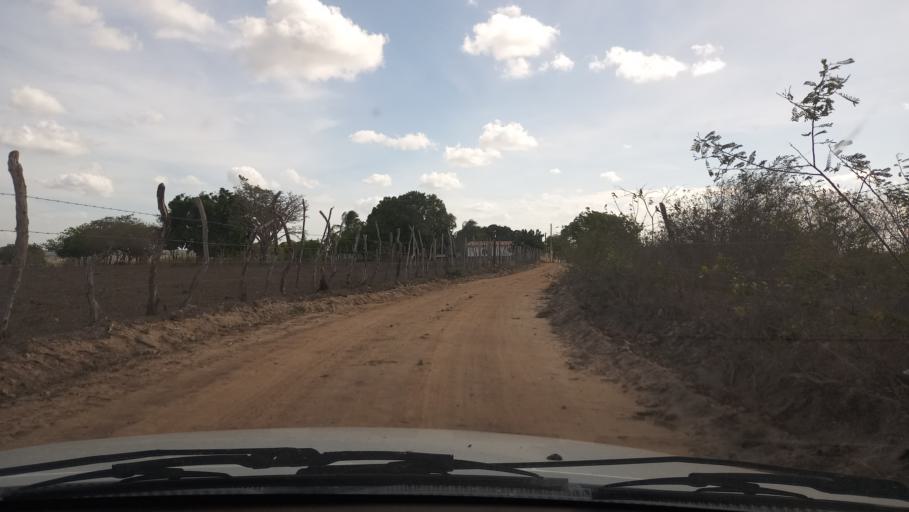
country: BR
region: Rio Grande do Norte
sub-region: Goianinha
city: Goianinha
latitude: -6.3167
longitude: -35.3075
